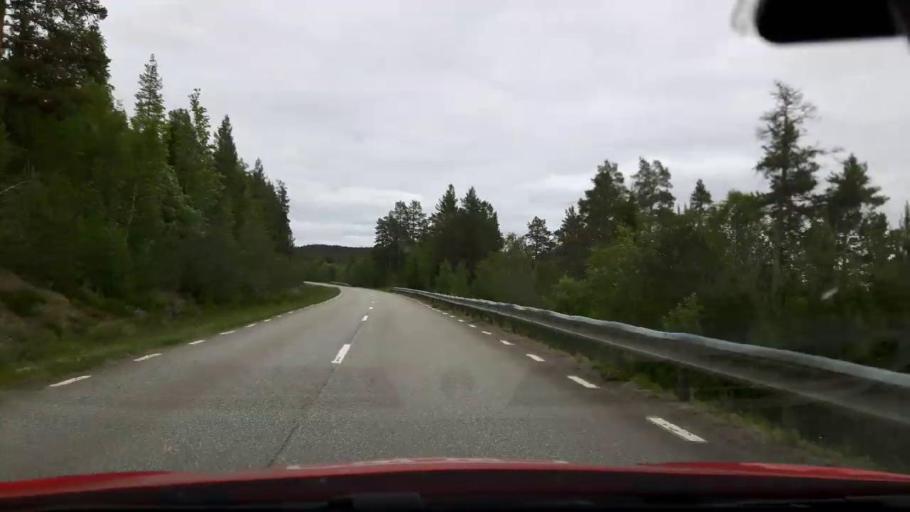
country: SE
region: Jaemtland
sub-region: Stroemsunds Kommun
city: Stroemsund
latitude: 63.3700
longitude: 15.7034
